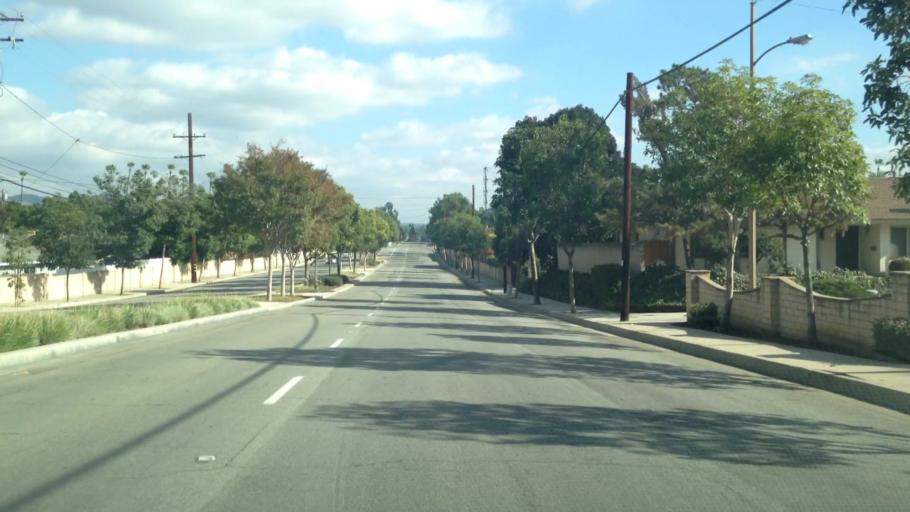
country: US
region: California
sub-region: Orange County
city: Yorba Linda
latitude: 33.8883
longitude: -117.8347
